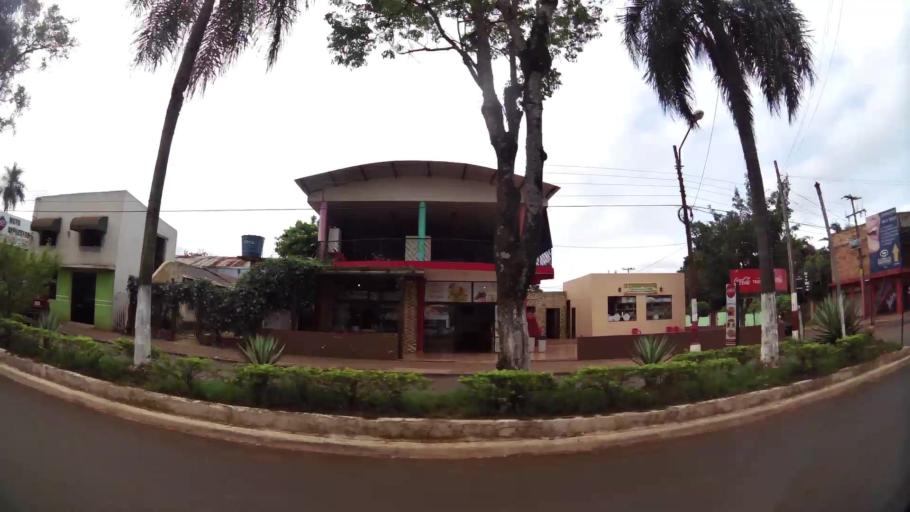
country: PY
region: Alto Parana
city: Ciudad del Este
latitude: -25.4061
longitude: -54.6402
